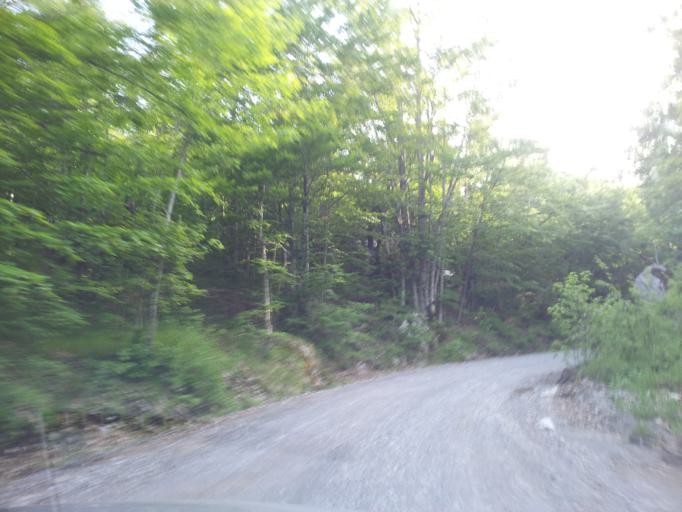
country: HR
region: Zadarska
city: Obrovac
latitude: 44.2995
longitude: 15.6609
